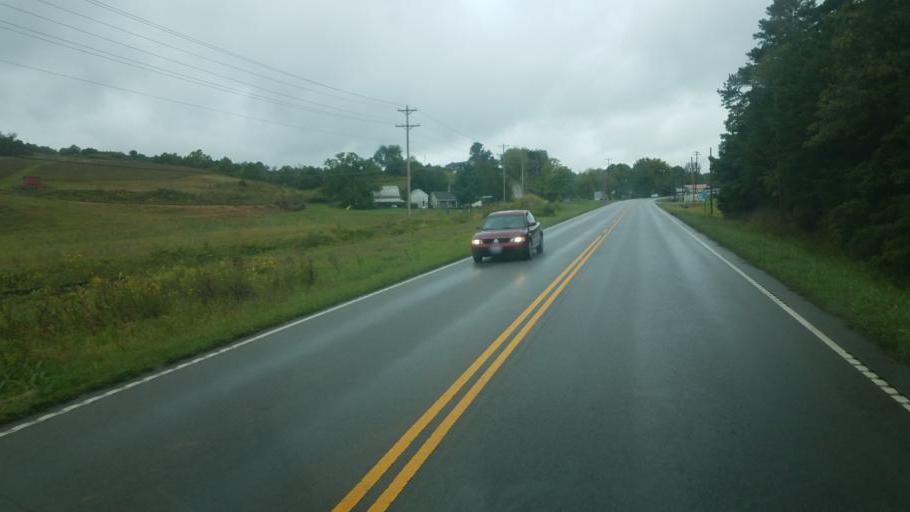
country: US
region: Ohio
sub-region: Scioto County
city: Wheelersburg
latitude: 38.8076
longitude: -82.7158
